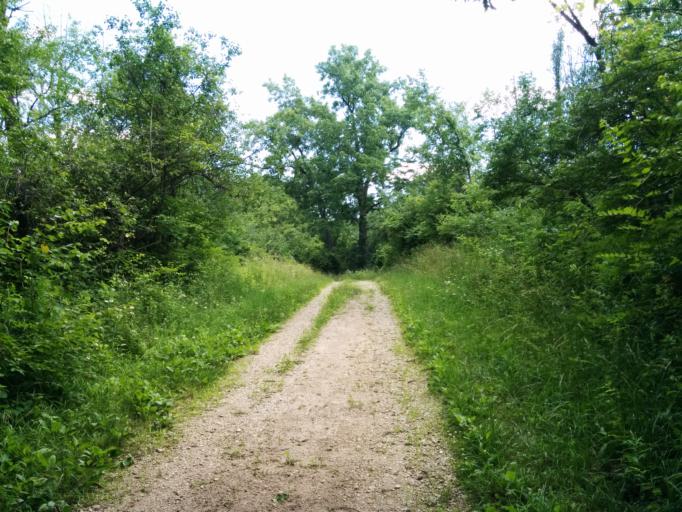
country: US
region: Illinois
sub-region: Will County
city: Goodings Grove
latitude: 41.6806
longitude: -87.8992
